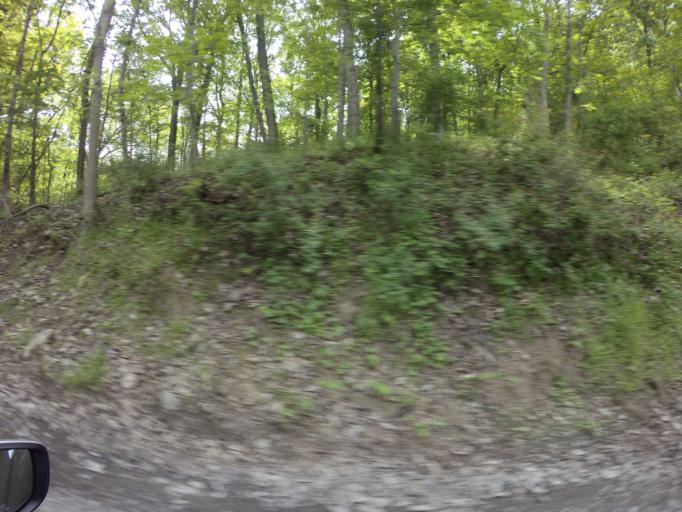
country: US
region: Maryland
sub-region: Carroll County
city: New Windsor
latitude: 39.4839
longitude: -77.0996
